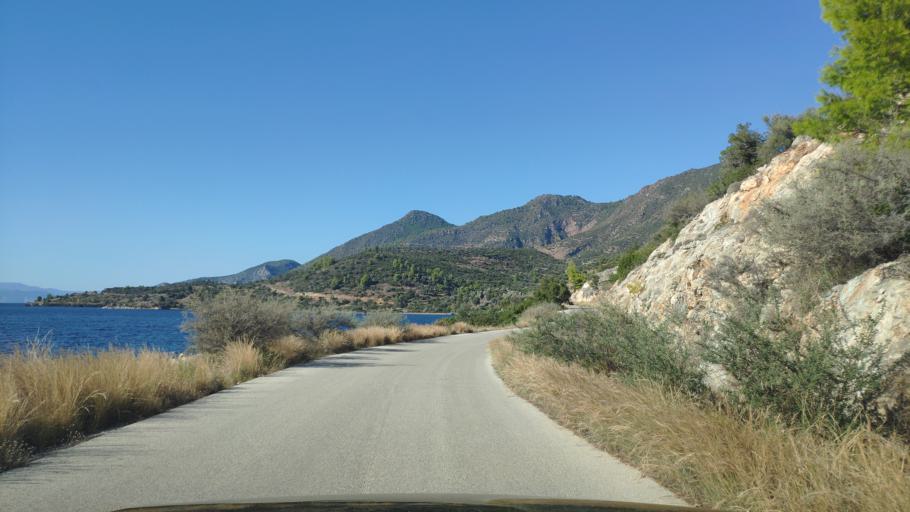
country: GR
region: Attica
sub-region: Nomos Piraios
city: Galatas
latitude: 37.5720
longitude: 23.3601
